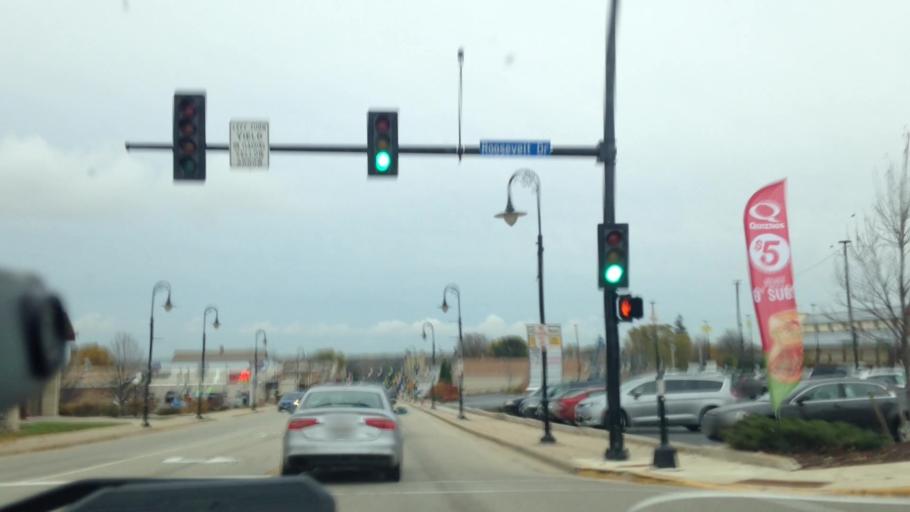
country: US
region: Wisconsin
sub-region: Waukesha County
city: Menomonee Falls
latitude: 43.1812
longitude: -88.1197
